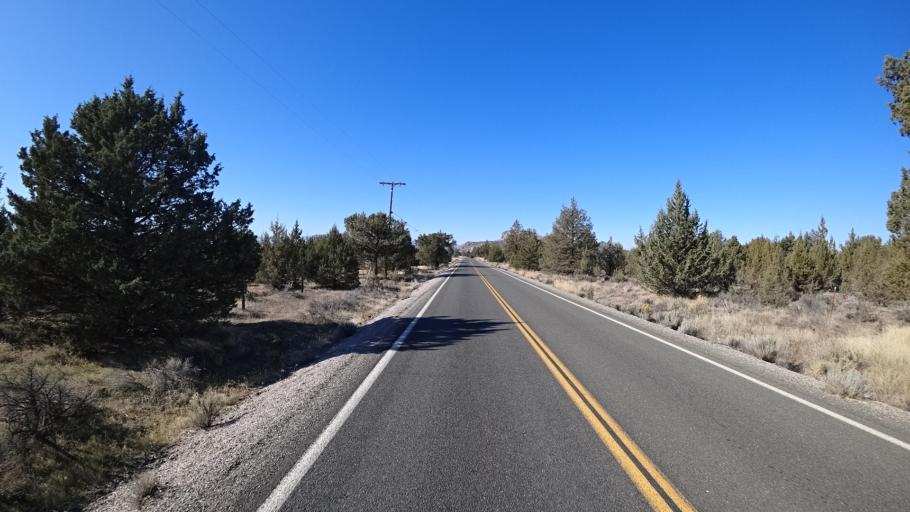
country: US
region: California
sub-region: Siskiyou County
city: Montague
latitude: 41.6599
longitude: -122.3884
